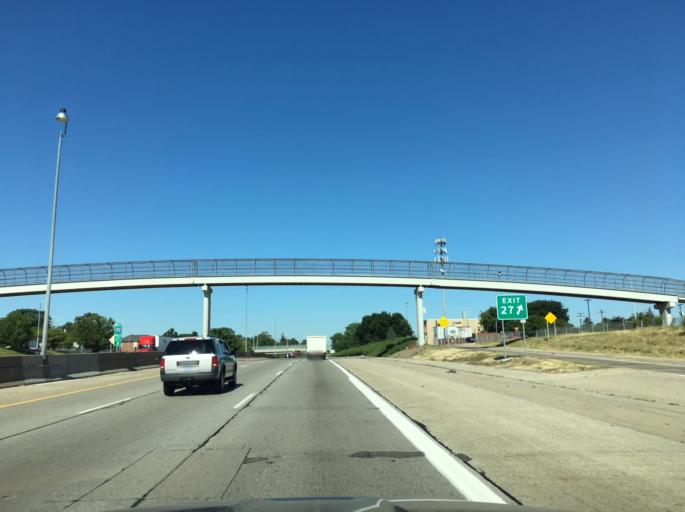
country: US
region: Michigan
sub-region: Macomb County
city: Roseville
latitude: 42.4946
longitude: -82.9338
